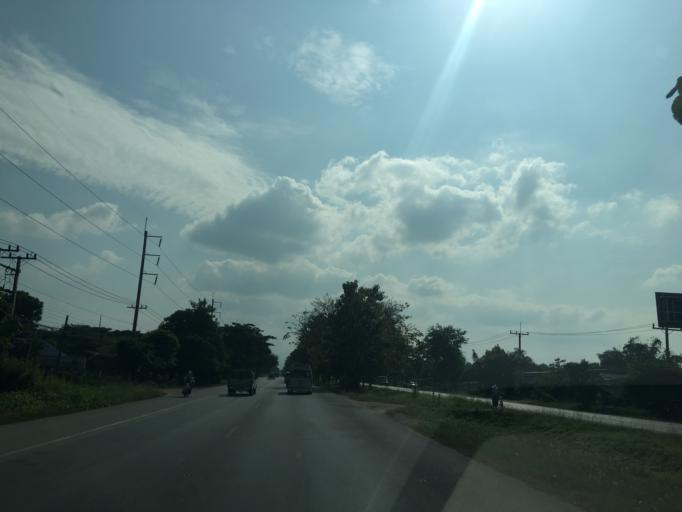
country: TH
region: Chiang Rai
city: Mae Lao
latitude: 19.7407
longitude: 99.7236
